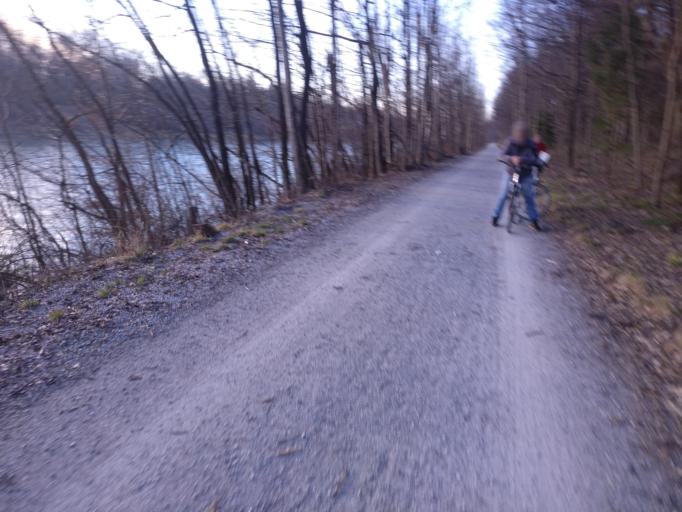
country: DE
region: Bavaria
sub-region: Upper Bavaria
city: Freilassing
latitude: 47.8560
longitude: 13.0011
